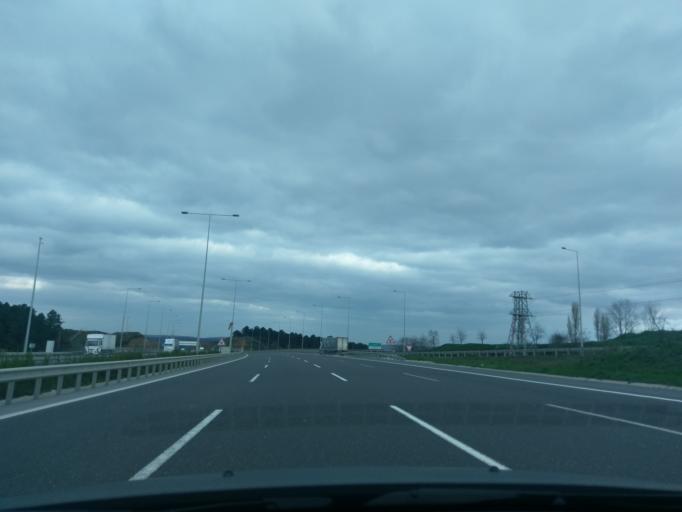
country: TR
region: Istanbul
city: Basaksehir
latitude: 41.1412
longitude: 28.8064
